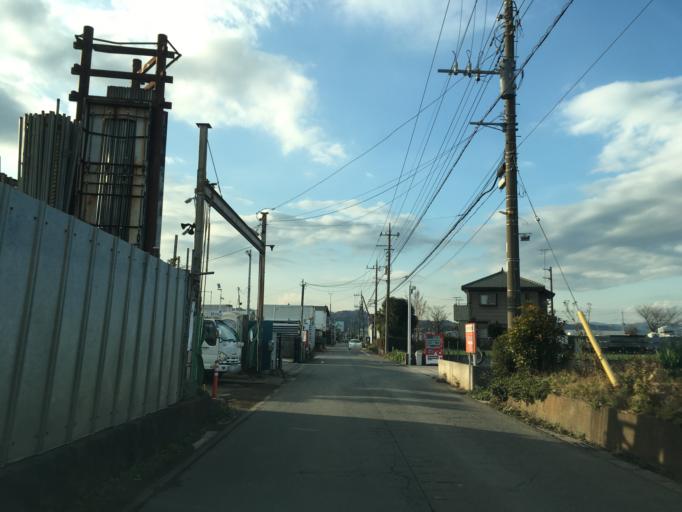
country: JP
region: Kanagawa
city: Zama
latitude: 35.5389
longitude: 139.3479
